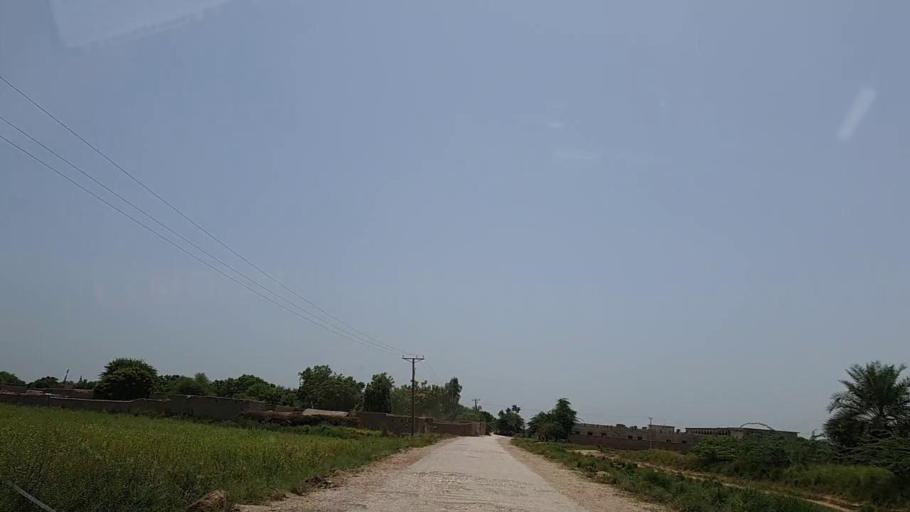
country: PK
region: Sindh
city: Tharu Shah
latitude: 26.9417
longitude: 68.1070
